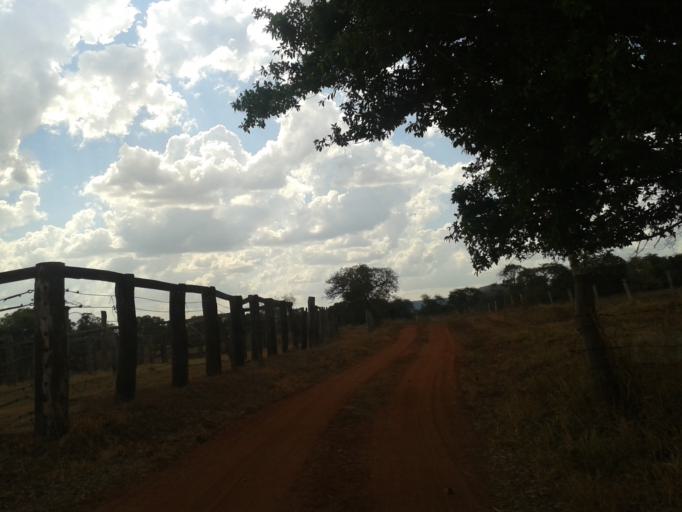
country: BR
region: Minas Gerais
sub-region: Santa Vitoria
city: Santa Vitoria
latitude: -19.1964
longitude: -49.9727
